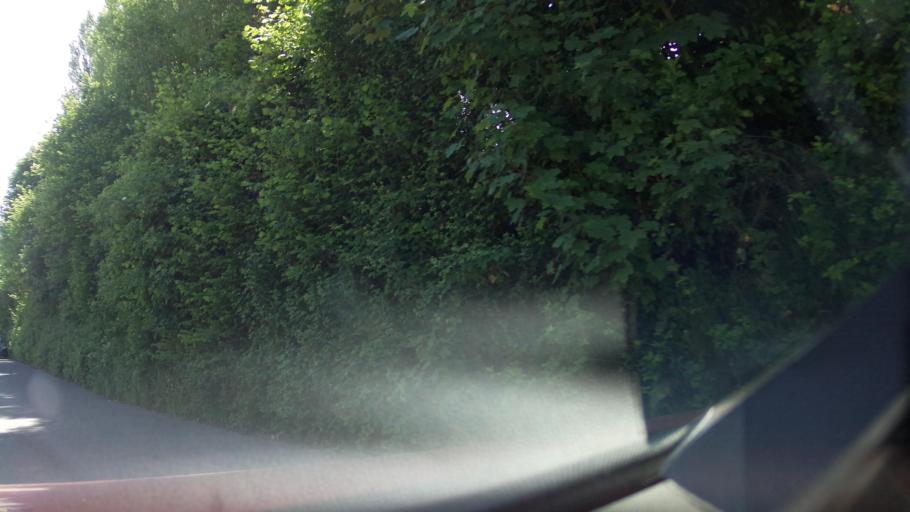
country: GB
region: England
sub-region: Devon
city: Ottery St Mary
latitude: 50.7519
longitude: -3.2704
